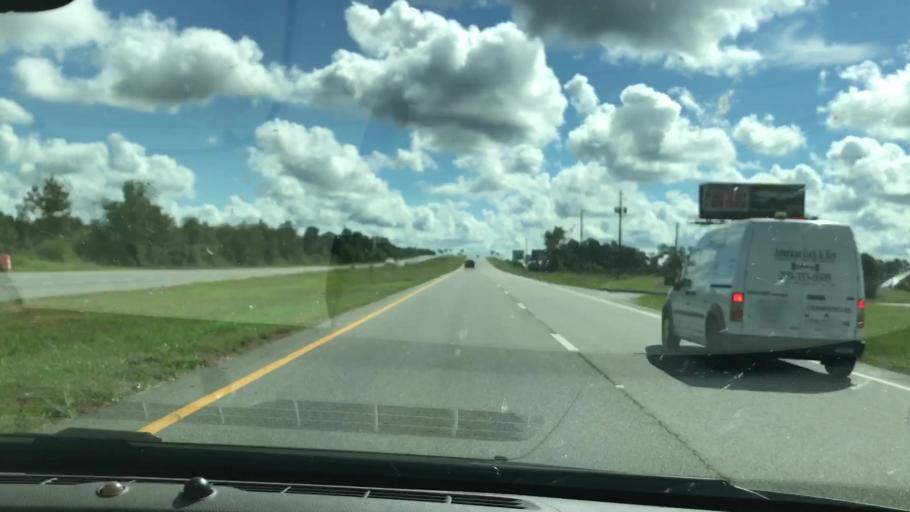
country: US
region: Georgia
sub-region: Lowndes County
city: Remerton
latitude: 30.8951
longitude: -83.3457
